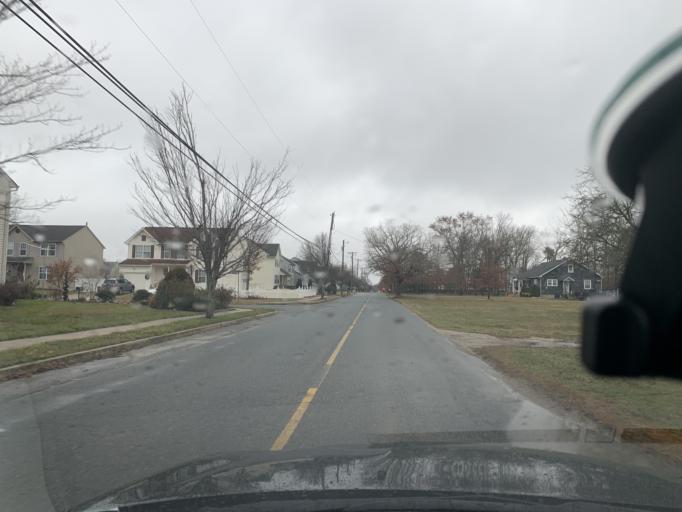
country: US
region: New Jersey
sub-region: Atlantic County
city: Pomona
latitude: 39.4287
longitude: -74.5870
